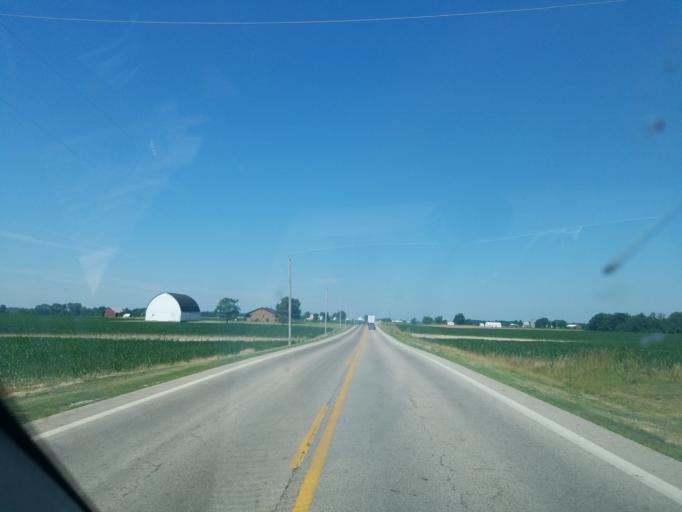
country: US
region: Ohio
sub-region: Shelby County
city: Botkins
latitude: 40.4385
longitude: -84.2164
